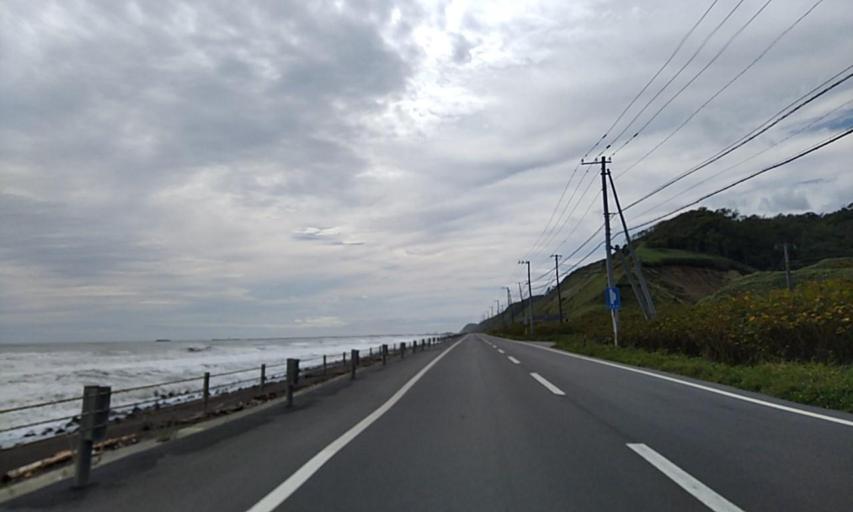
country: JP
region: Hokkaido
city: Kushiro
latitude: 42.8191
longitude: 143.8355
